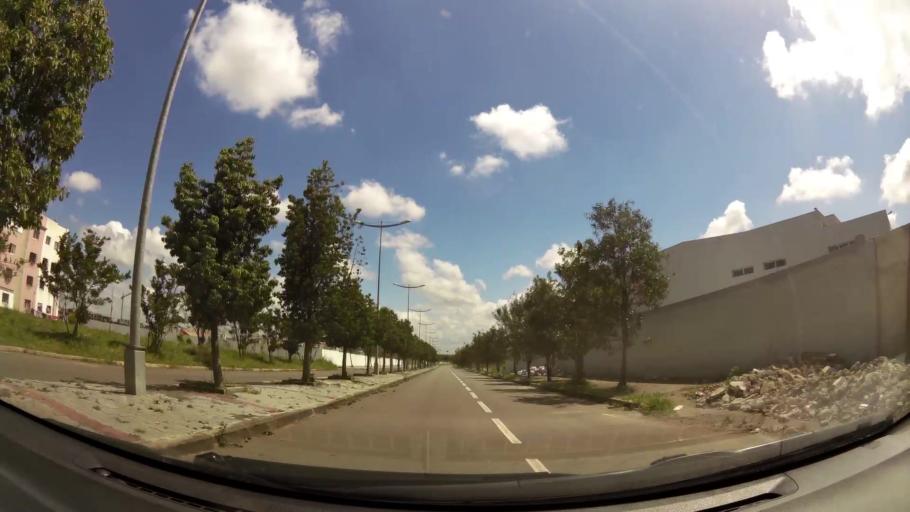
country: MA
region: Grand Casablanca
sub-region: Nouaceur
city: Dar Bouazza
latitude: 33.4218
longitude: -7.8374
